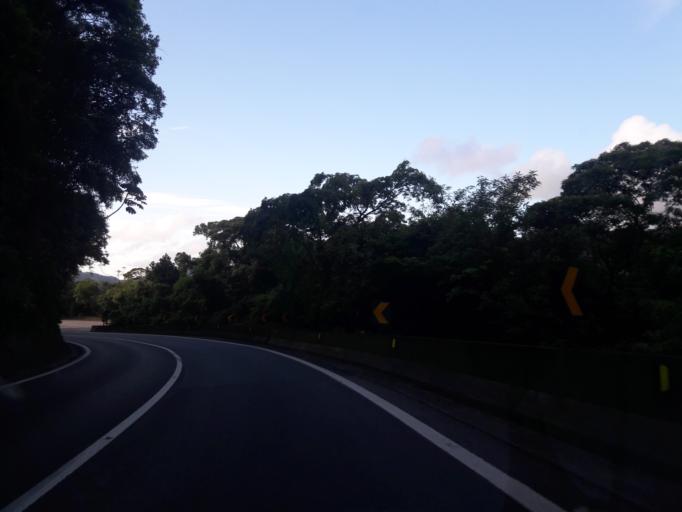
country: BR
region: Sao Paulo
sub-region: Cubatao
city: Cubatao
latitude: -23.8898
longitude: -46.4931
